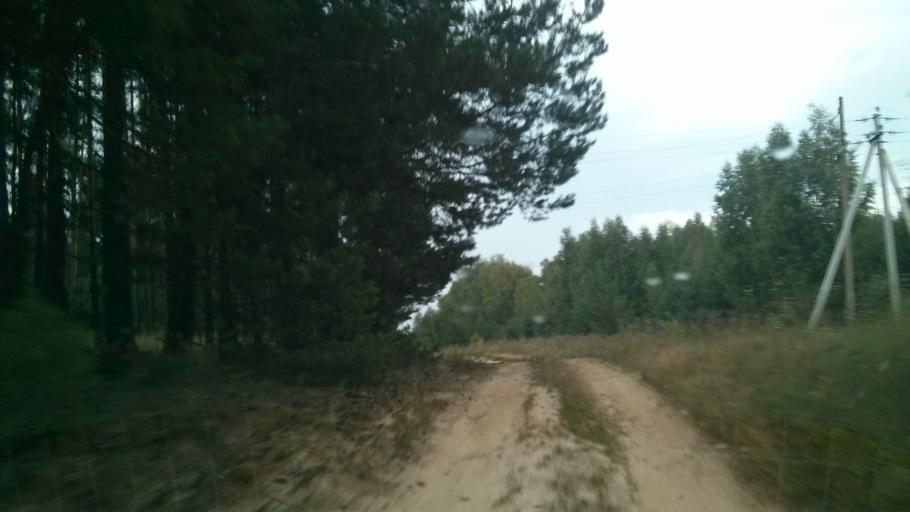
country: RU
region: Nizjnij Novgorod
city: Shimorskoye
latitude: 55.3082
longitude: 41.8593
